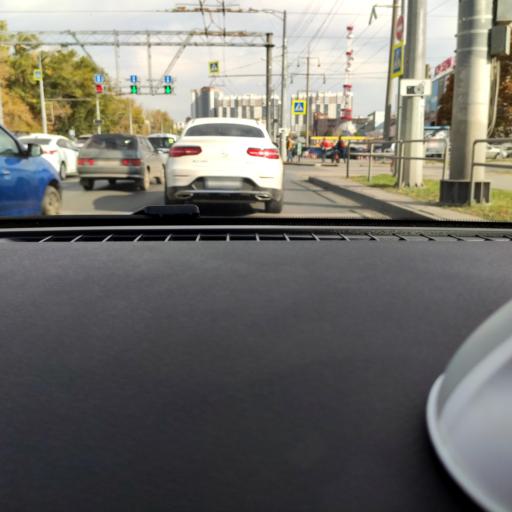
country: RU
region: Samara
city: Samara
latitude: 53.2140
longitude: 50.1796
